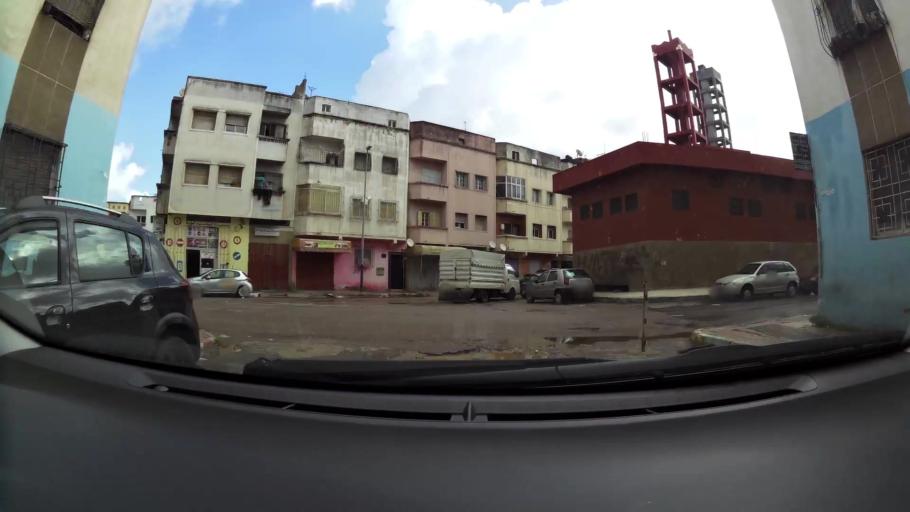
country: MA
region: Grand Casablanca
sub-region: Mediouna
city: Tit Mellil
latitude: 33.5935
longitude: -7.5165
